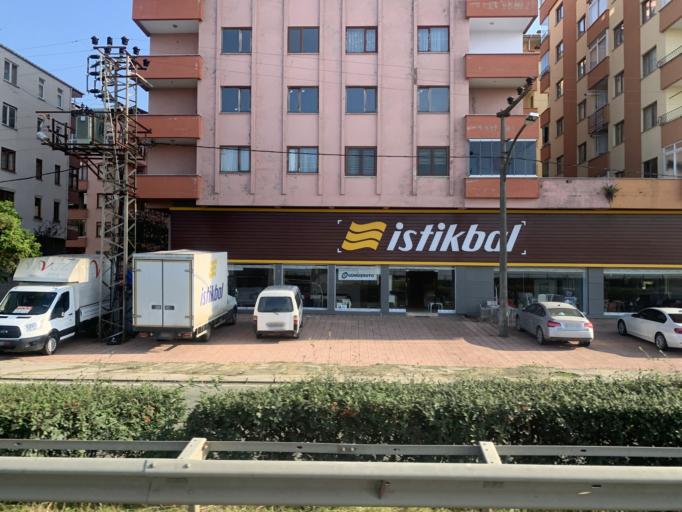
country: TR
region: Trabzon
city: Of
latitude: 40.9417
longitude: 40.2588
